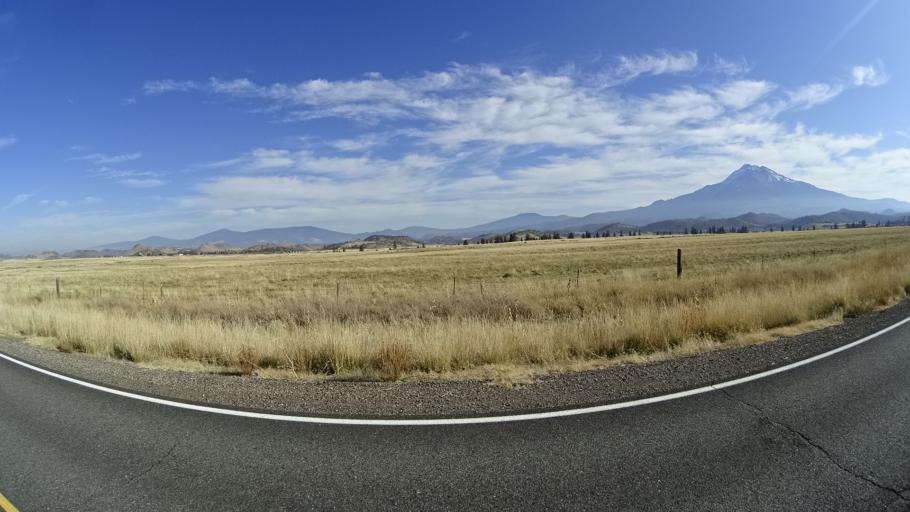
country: US
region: California
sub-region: Siskiyou County
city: Weed
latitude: 41.4621
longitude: -122.4639
